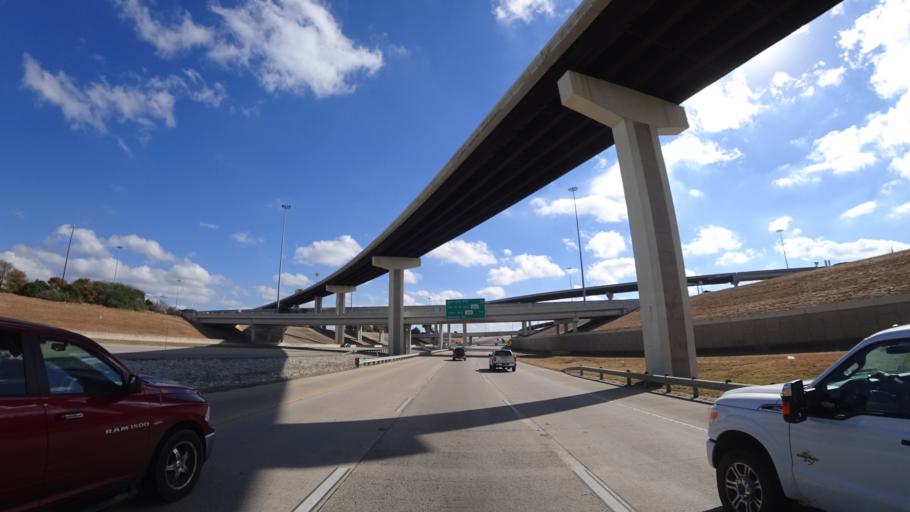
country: US
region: Texas
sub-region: Travis County
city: Rollingwood
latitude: 30.2360
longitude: -97.8264
